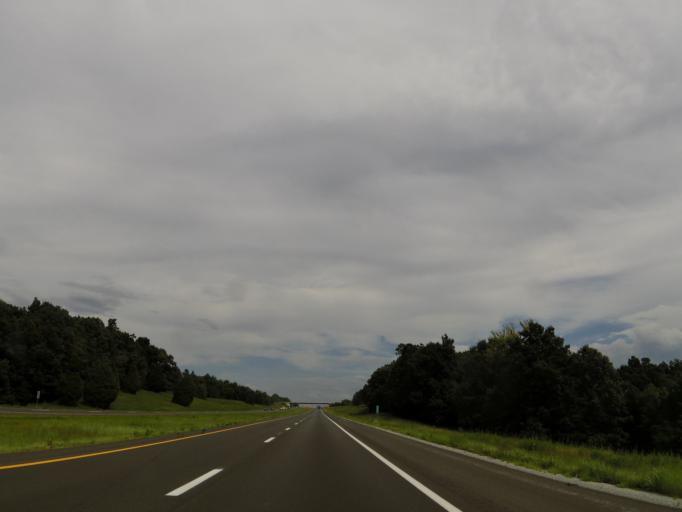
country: US
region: Kentucky
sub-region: Marshall County
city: Calvert City
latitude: 36.9907
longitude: -88.3835
